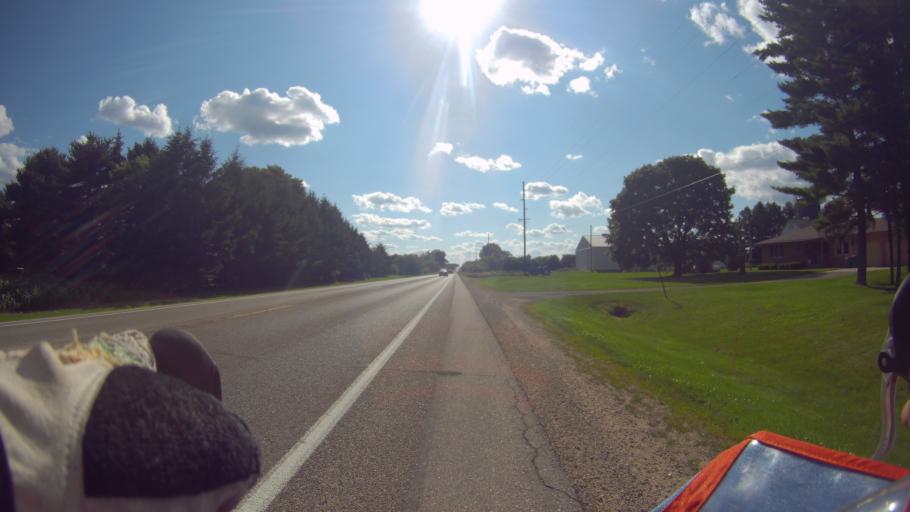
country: US
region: Wisconsin
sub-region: Dane County
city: Oregon
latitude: 42.9190
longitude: -89.3107
